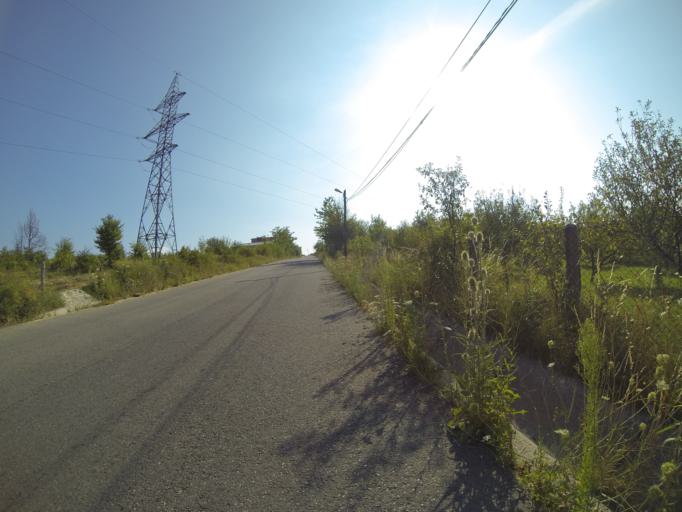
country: RO
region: Valcea
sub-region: Comuna Horezu
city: Horezu
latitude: 45.1503
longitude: 24.0021
